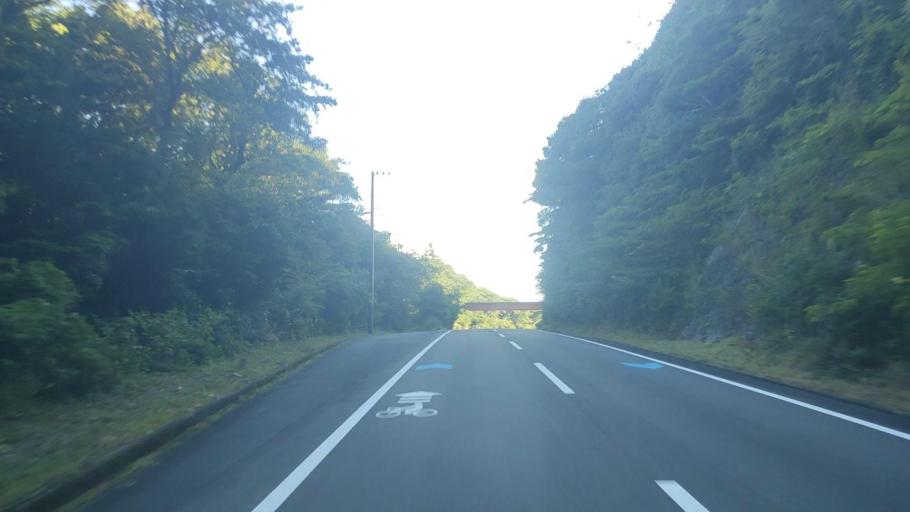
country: JP
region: Mie
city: Toba
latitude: 34.4011
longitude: 136.8742
